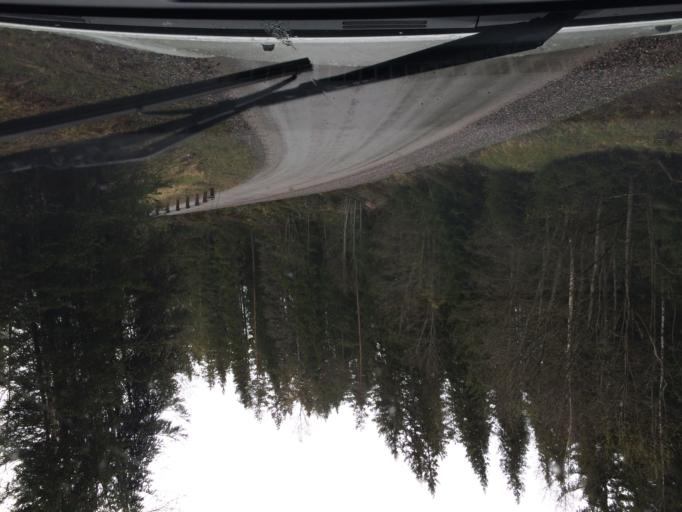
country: SE
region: Dalarna
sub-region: Ludvika Kommun
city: Abborrberget
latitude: 60.0226
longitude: 14.6086
